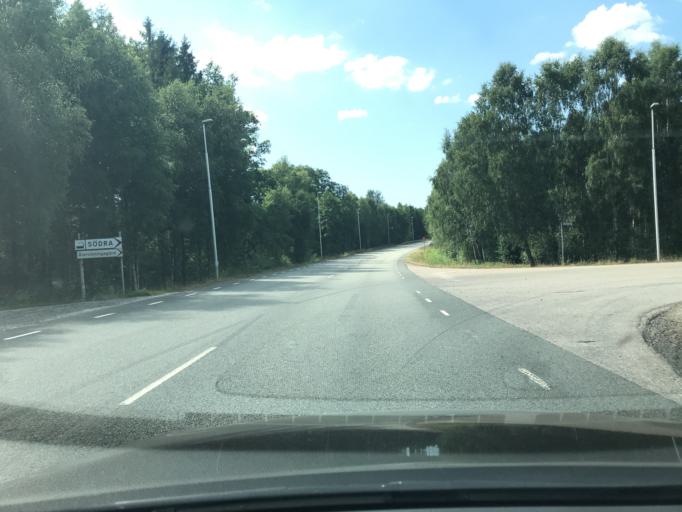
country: SE
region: Skane
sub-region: Hassleholms Kommun
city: Hastveda
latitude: 56.2769
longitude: 13.9388
